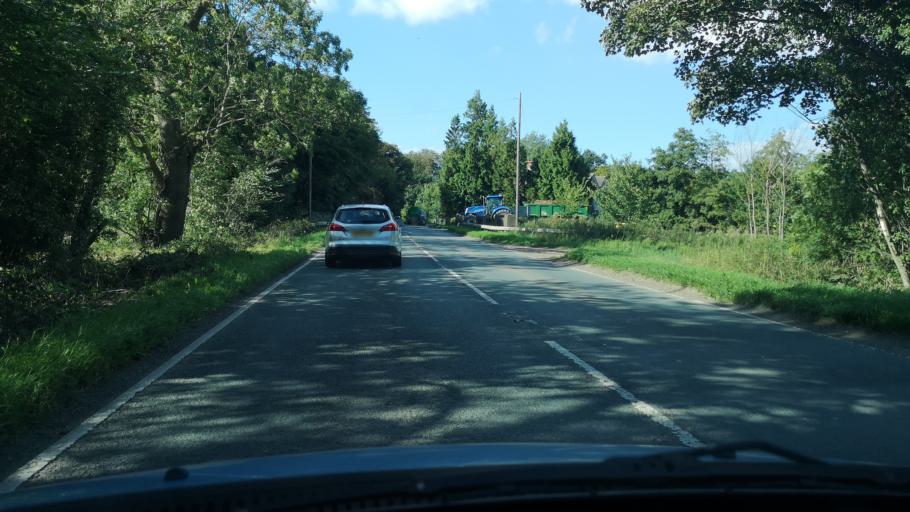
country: GB
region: England
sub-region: North Lincolnshire
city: Belton
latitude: 53.5780
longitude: -0.8199
